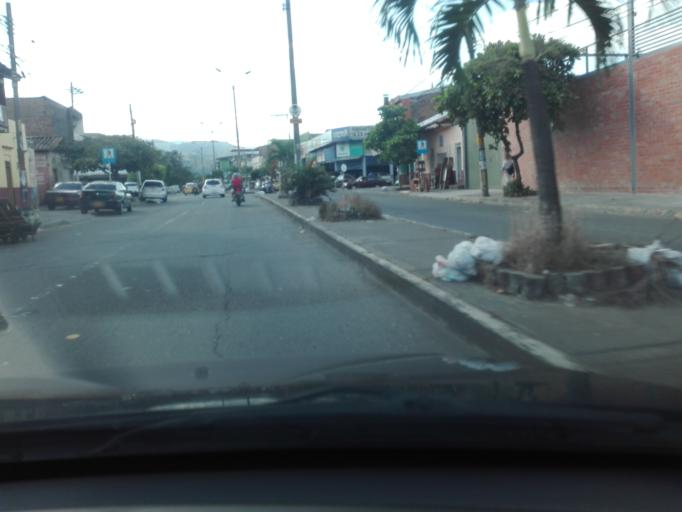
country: CO
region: Valle del Cauca
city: Cali
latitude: 3.4410
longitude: -76.5159
